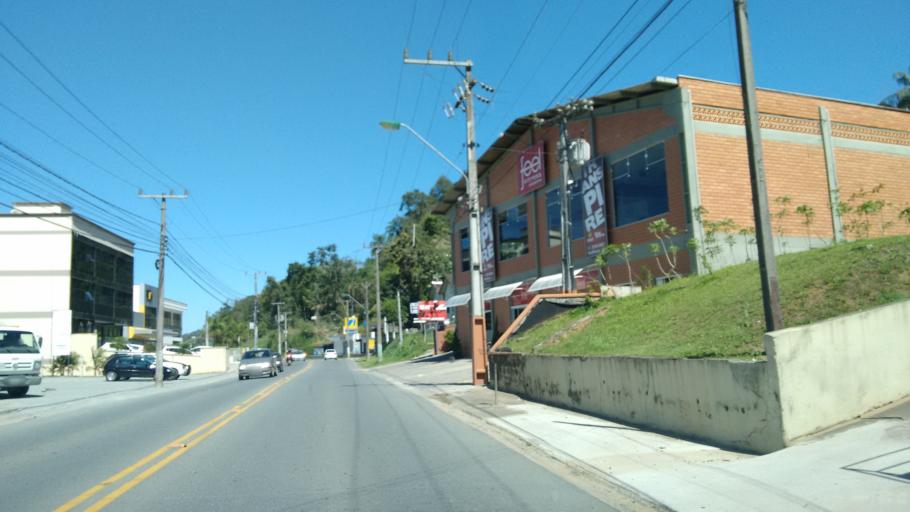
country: BR
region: Santa Catarina
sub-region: Blumenau
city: Blumenau
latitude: -26.8747
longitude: -49.1036
